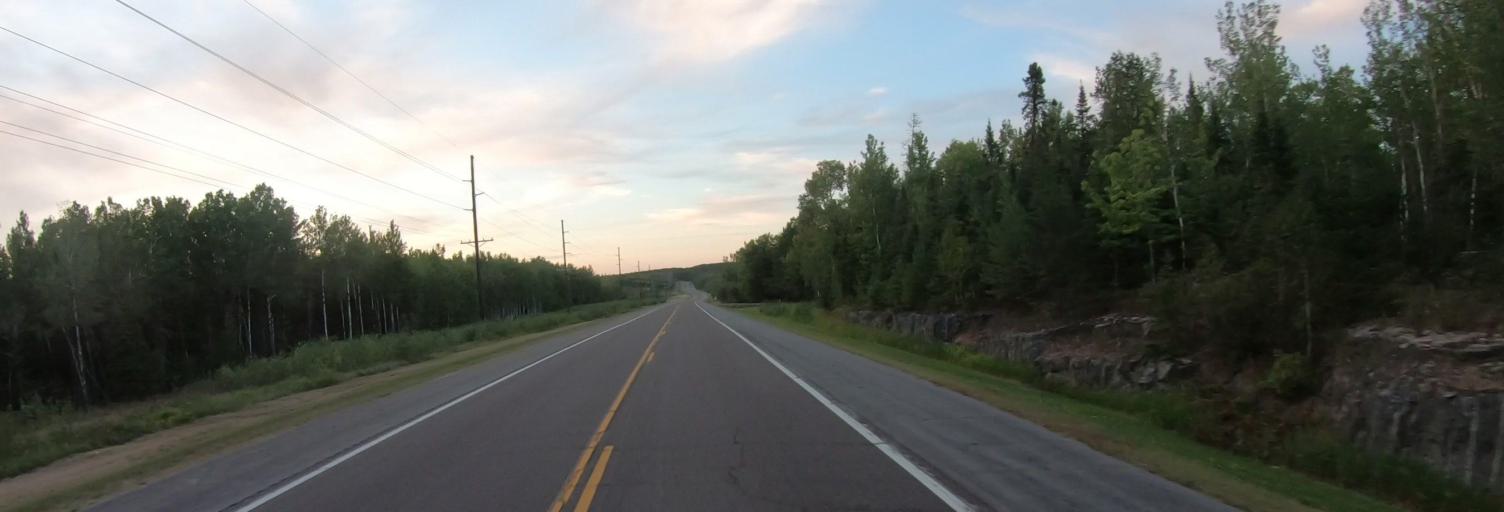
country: US
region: Minnesota
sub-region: Saint Louis County
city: Aurora
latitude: 47.8264
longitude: -92.3728
